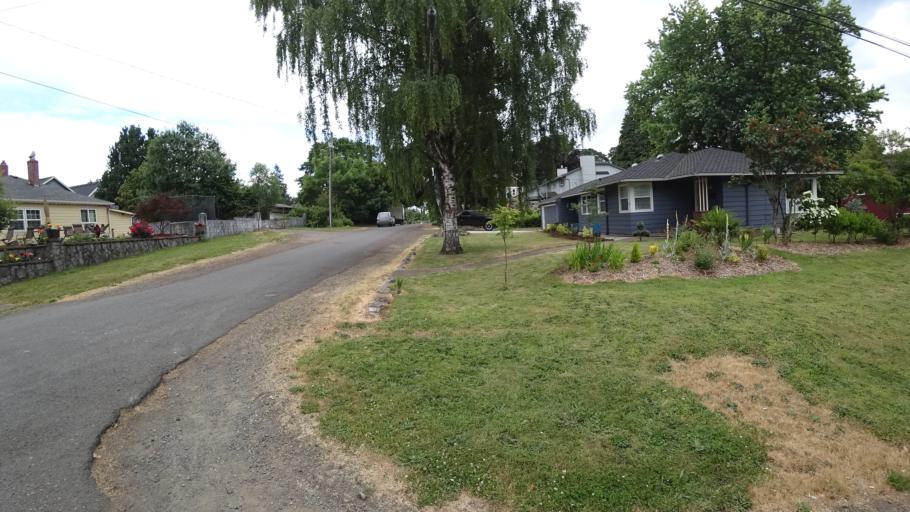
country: US
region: Oregon
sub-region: Washington County
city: West Haven
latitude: 45.5832
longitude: -122.7503
